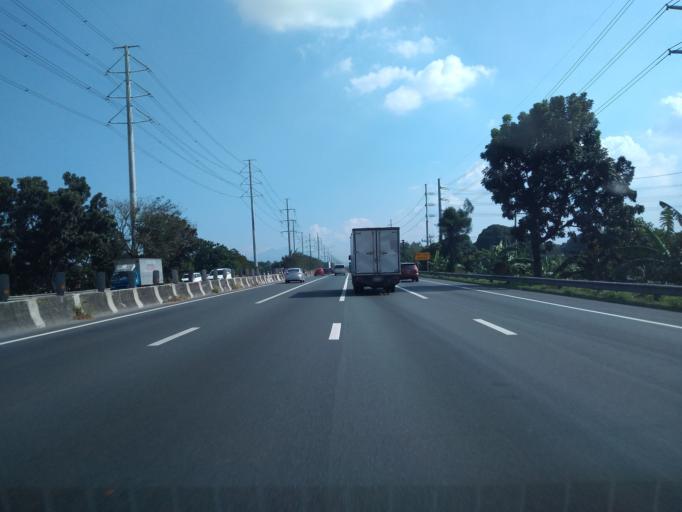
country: PH
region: Calabarzon
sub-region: Province of Laguna
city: Pulong Santa Cruz
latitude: 14.2910
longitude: 121.0855
